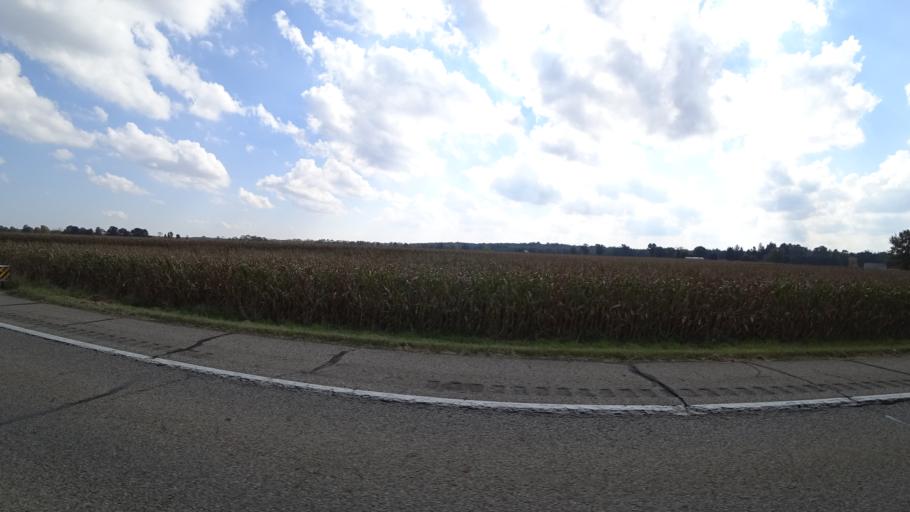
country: US
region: Michigan
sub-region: Branch County
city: Union City
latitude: 42.1059
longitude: -85.0266
